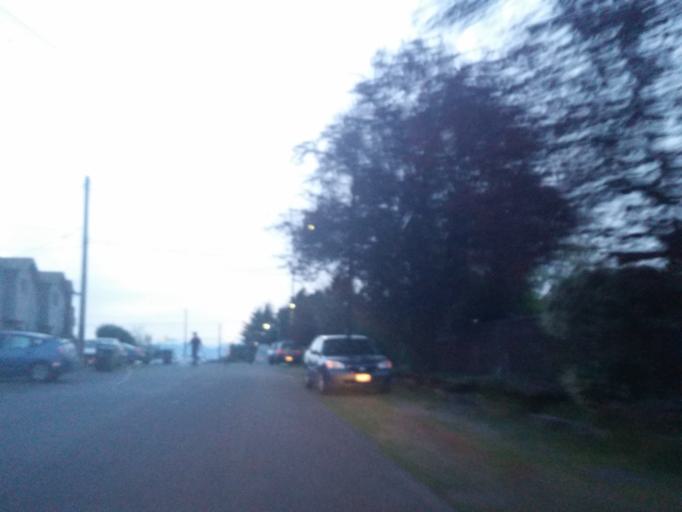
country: US
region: Washington
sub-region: King County
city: Shoreline
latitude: 47.7106
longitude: -122.3530
